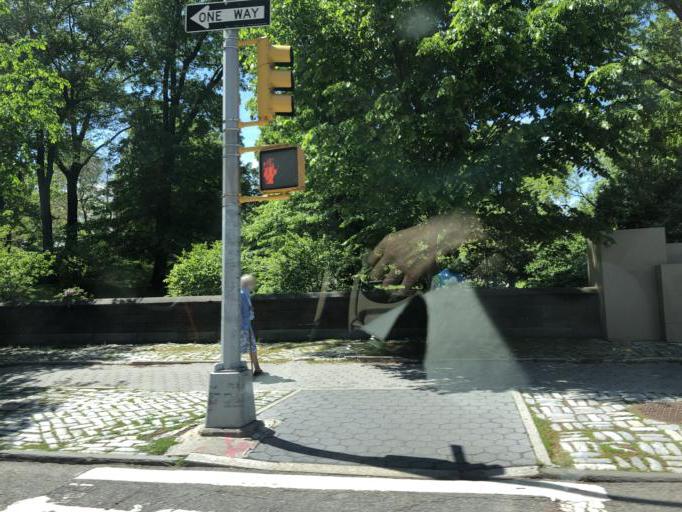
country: US
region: New York
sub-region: New York County
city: Manhattan
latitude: 40.7923
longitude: -73.9526
